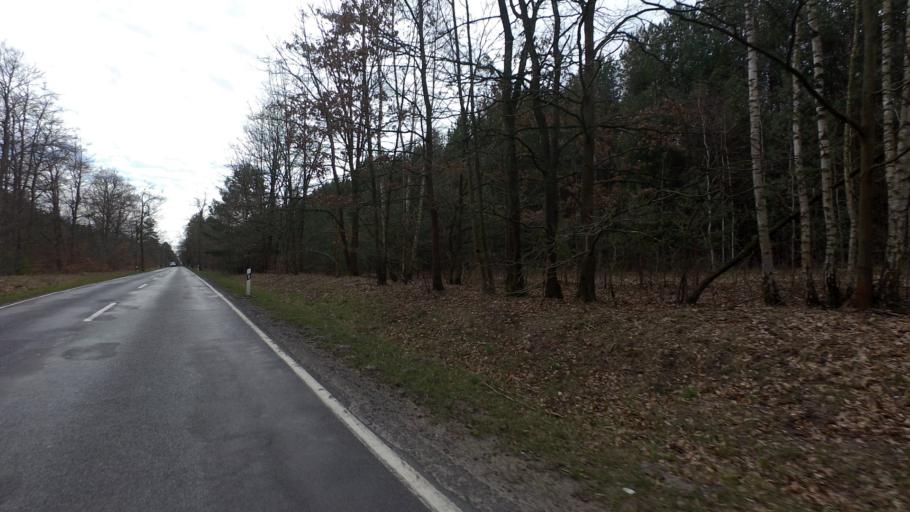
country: DE
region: Brandenburg
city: Wandlitz
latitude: 52.7295
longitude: 13.3680
